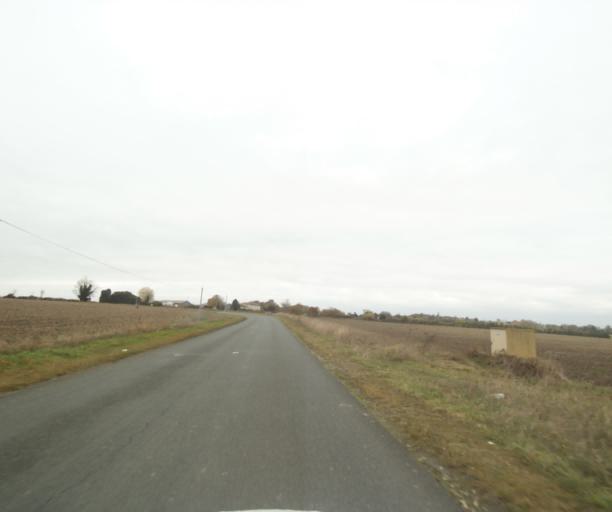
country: FR
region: Poitou-Charentes
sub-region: Departement de la Charente-Maritime
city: Saintes
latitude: 45.7307
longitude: -0.6656
